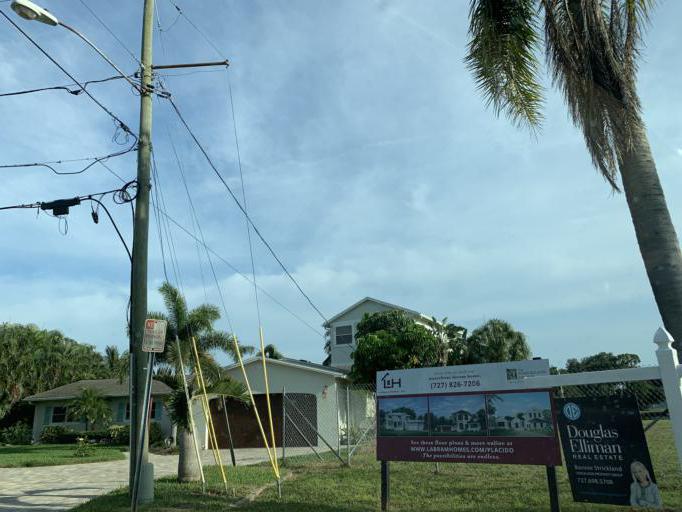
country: US
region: Florida
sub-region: Pinellas County
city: Lealman
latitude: 27.8049
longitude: -82.6258
